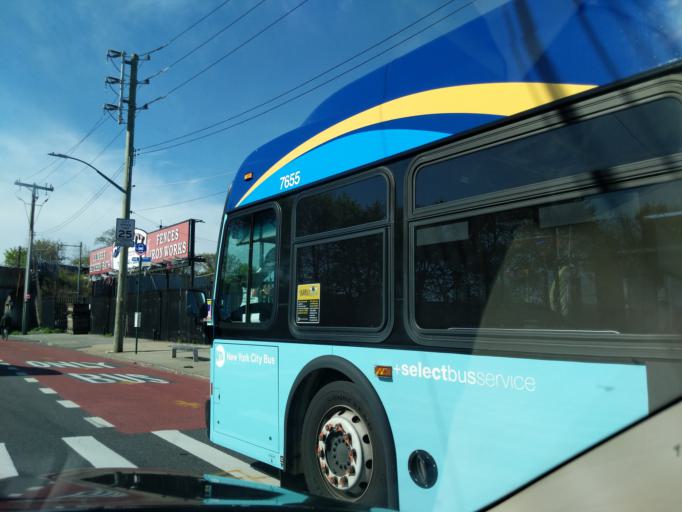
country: US
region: New York
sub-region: Kings County
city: Brooklyn
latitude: 40.6374
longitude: -73.9289
